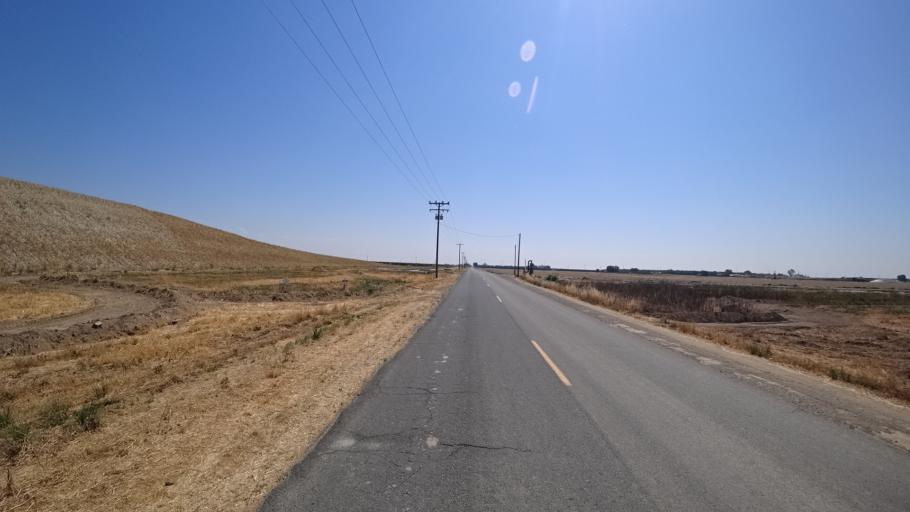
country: US
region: California
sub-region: Kings County
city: Hanford
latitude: 36.3718
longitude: -119.5913
